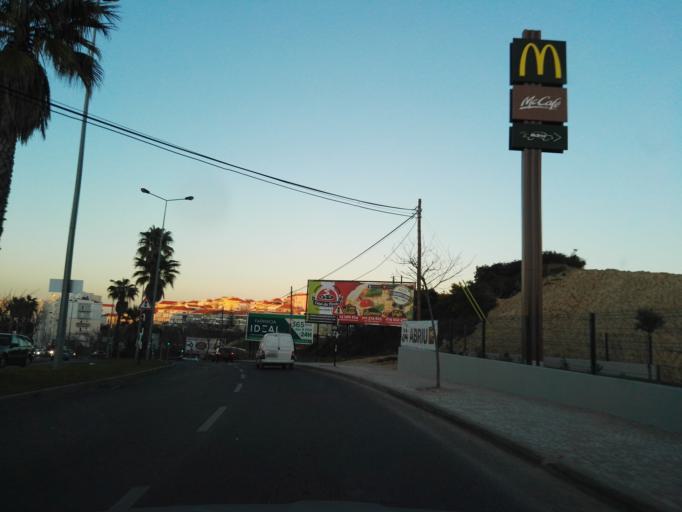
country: PT
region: Setubal
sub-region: Almada
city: Piedade
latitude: 38.6631
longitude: -9.1628
